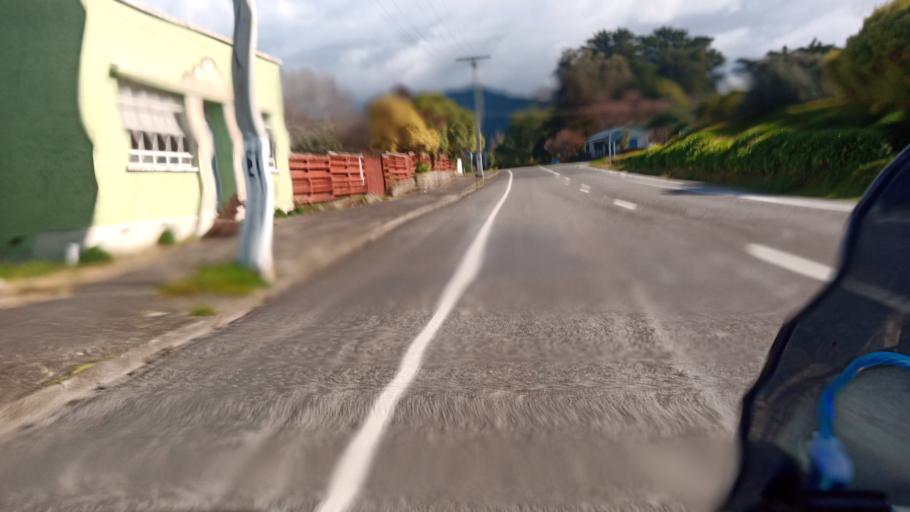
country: NZ
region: Gisborne
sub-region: Gisborne District
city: Gisborne
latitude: -38.1266
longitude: 178.3162
